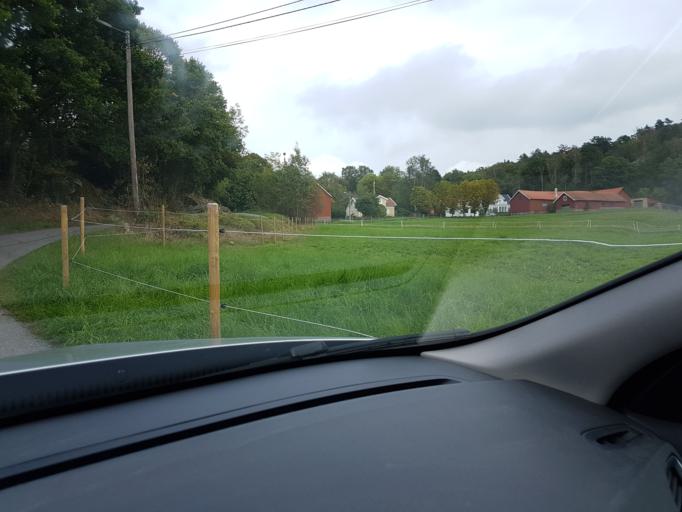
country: SE
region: Vaestra Goetaland
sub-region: Ale Kommun
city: Surte
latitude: 57.8550
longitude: 12.0287
